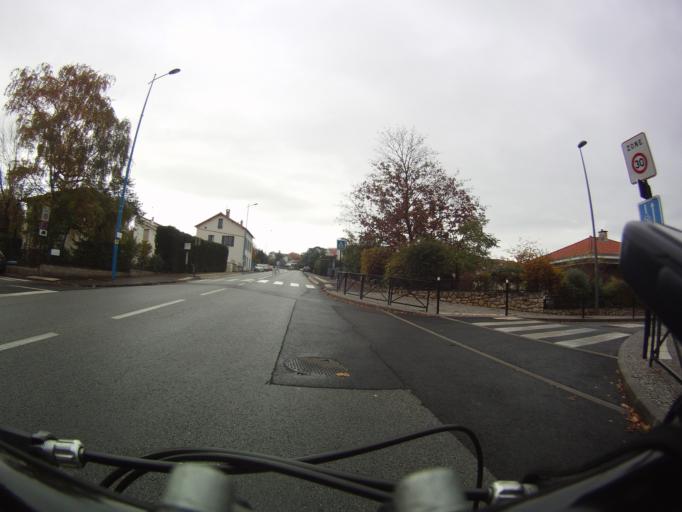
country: FR
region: Auvergne
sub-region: Departement du Puy-de-Dome
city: Aubiere
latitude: 45.7522
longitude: 3.1081
